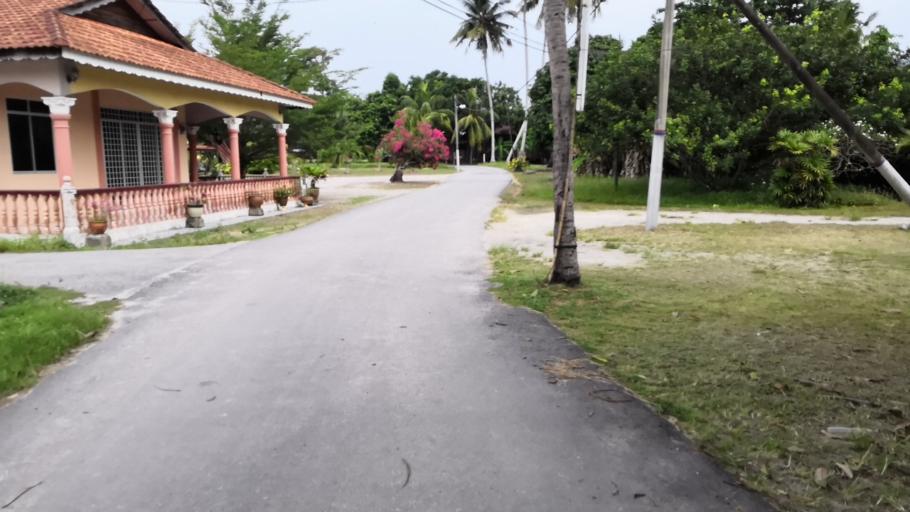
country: MY
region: Perak
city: Lumut
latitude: 4.2975
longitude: 100.6706
